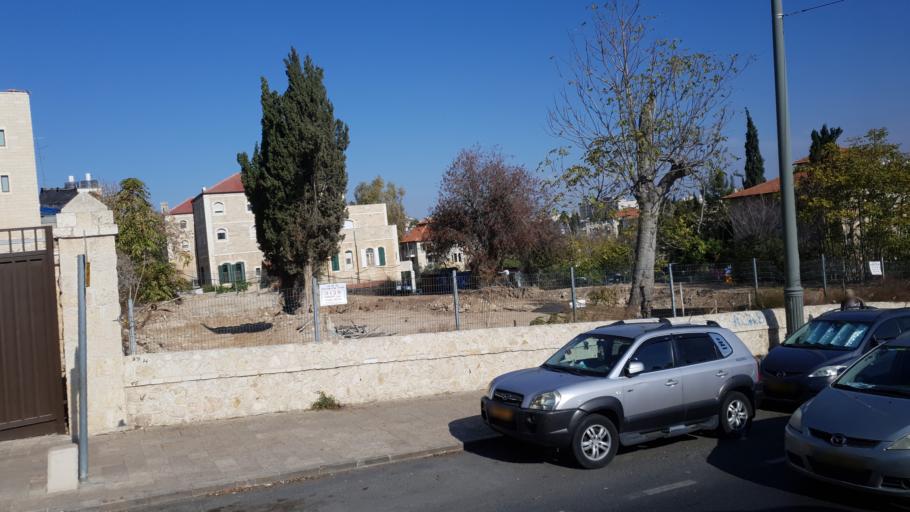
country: PS
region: West Bank
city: East Jerusalem
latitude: 31.7802
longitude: 35.2270
